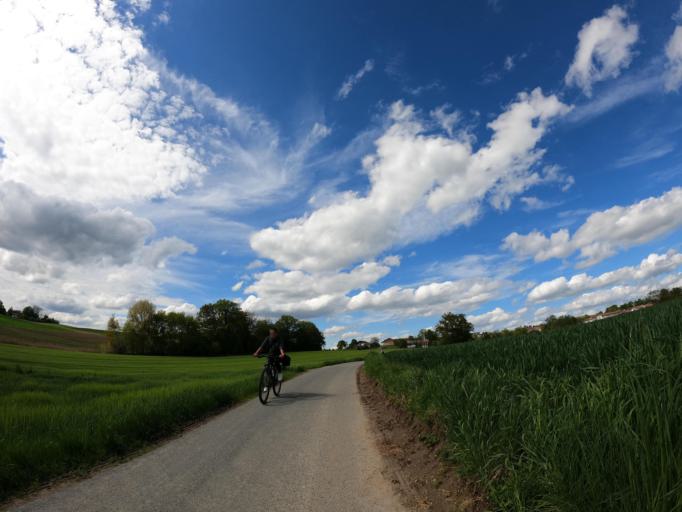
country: DE
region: Bavaria
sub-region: Upper Bavaria
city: Ebersberg
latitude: 48.0665
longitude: 11.9544
